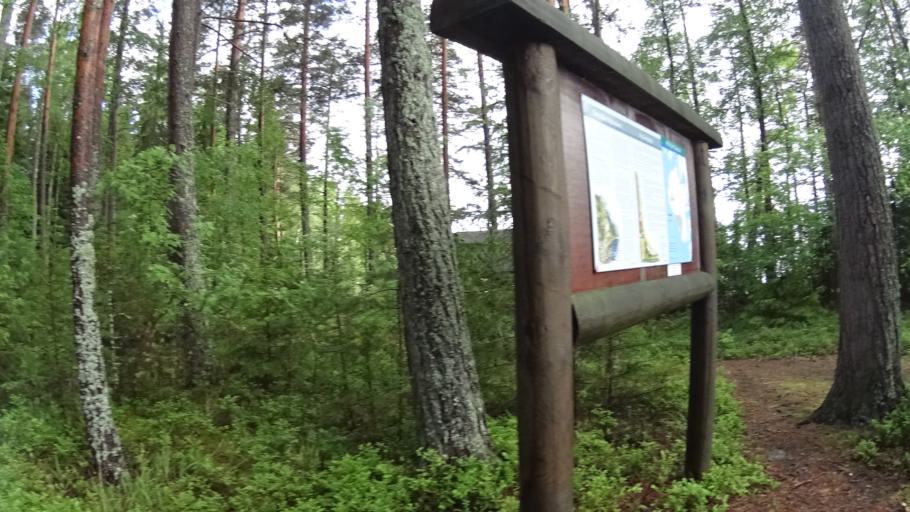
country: FI
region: Paijanne Tavastia
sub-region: Lahti
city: Sysmae
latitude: 61.4824
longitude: 25.5615
